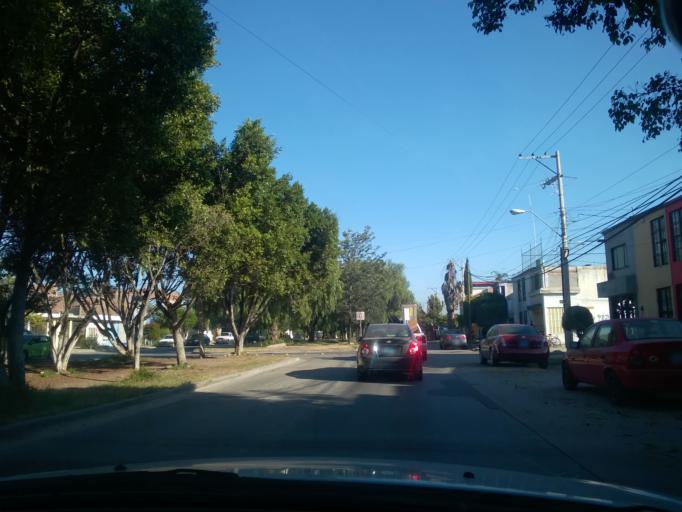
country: MX
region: Guanajuato
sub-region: Leon
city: San Jose de Duran (Los Troncoso)
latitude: 21.0752
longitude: -101.6450
